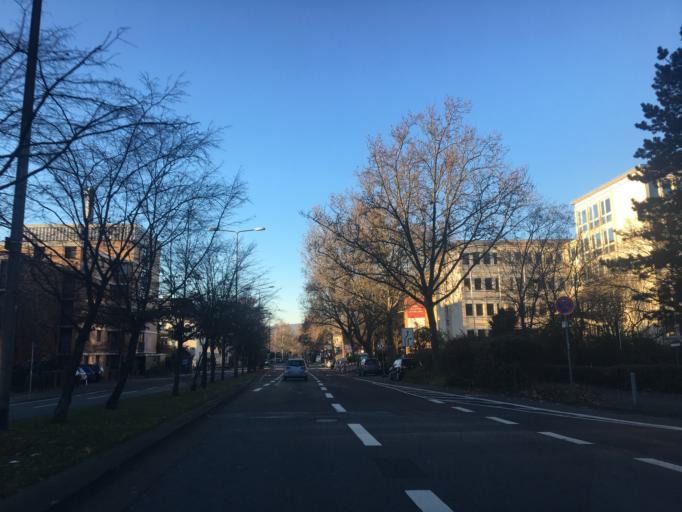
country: DE
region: Hesse
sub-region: Regierungsbezirk Darmstadt
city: Wiesbaden
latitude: 50.0736
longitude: 8.2555
